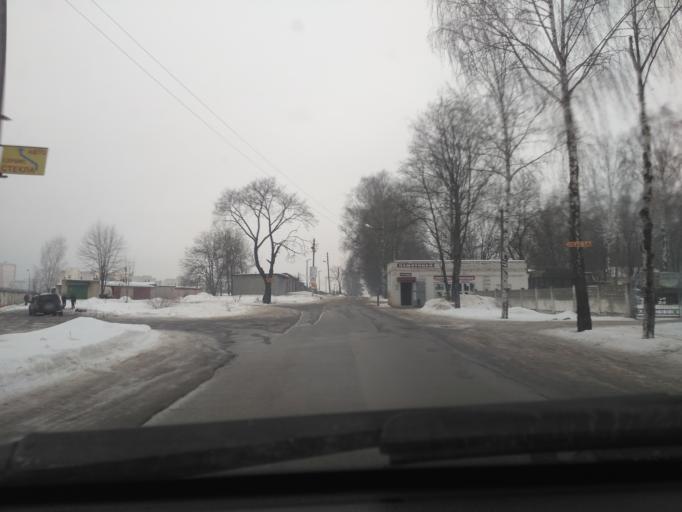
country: BY
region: Minsk
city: Horad Barysaw
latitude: 54.2204
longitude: 28.4812
